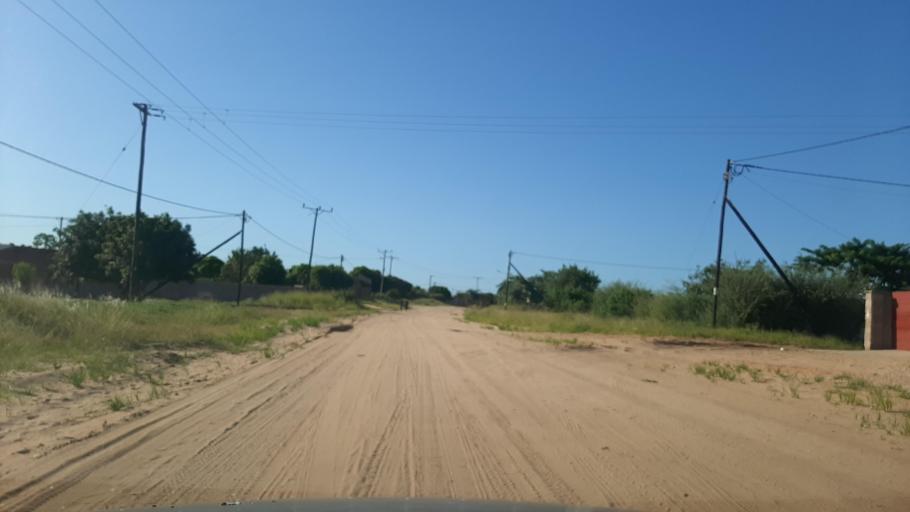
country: MZ
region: Maputo City
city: Maputo
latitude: -25.7657
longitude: 32.5474
